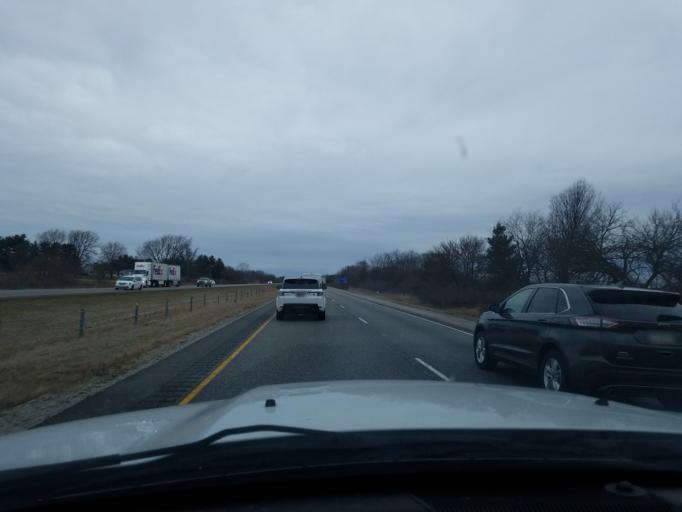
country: US
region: Indiana
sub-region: Tippecanoe County
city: Dayton
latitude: 40.3497
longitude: -86.7693
